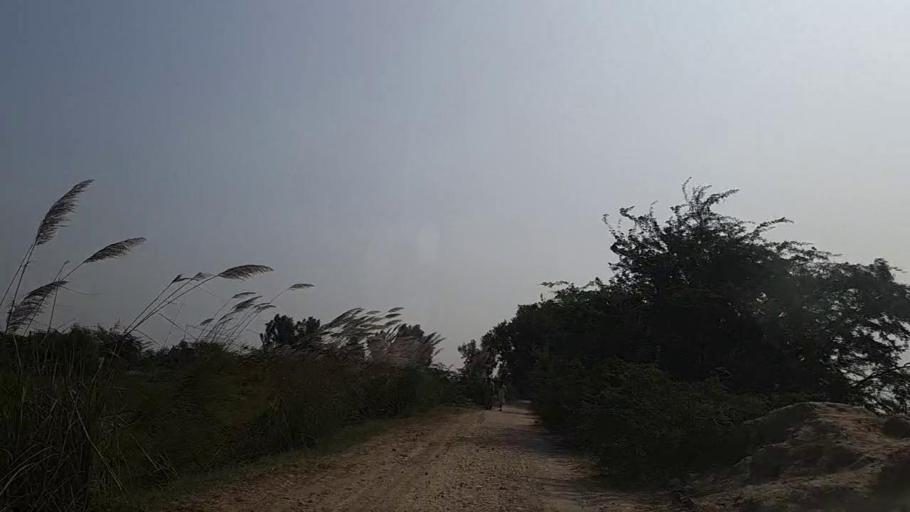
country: PK
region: Sindh
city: Mirpur Sakro
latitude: 24.5927
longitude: 67.7181
